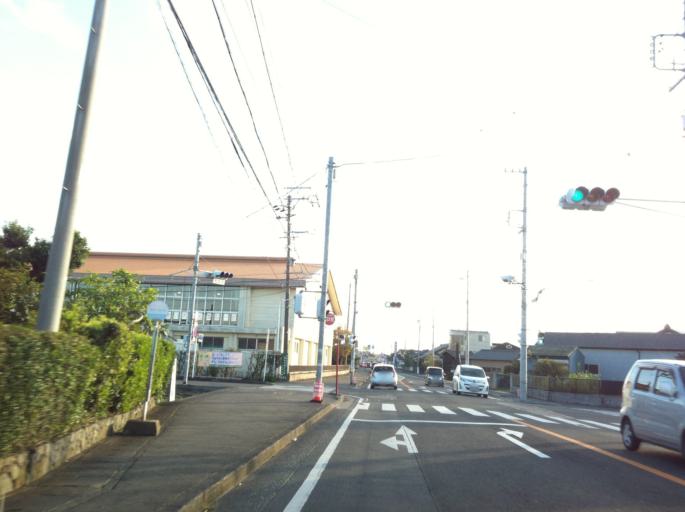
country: JP
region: Shizuoka
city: Fujieda
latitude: 34.8441
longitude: 138.2693
